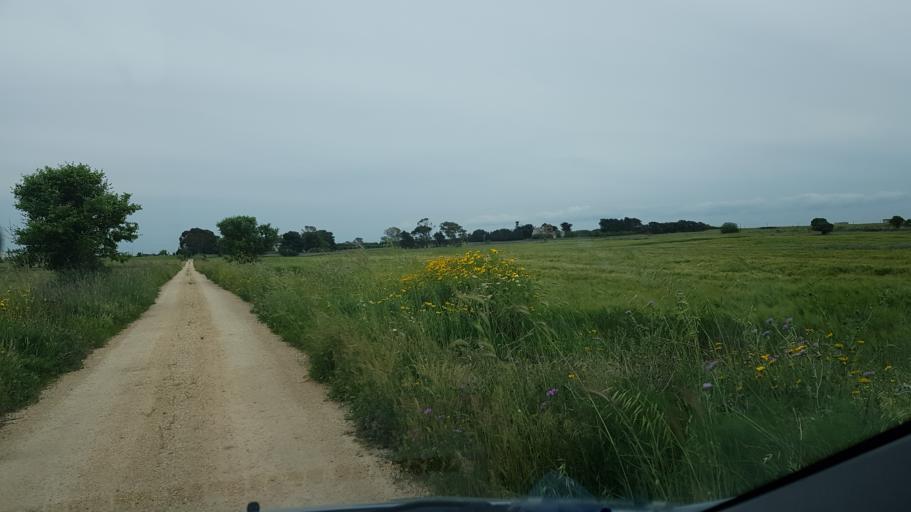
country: IT
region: Apulia
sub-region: Provincia di Brindisi
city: Brindisi
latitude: 40.6530
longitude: 17.8822
